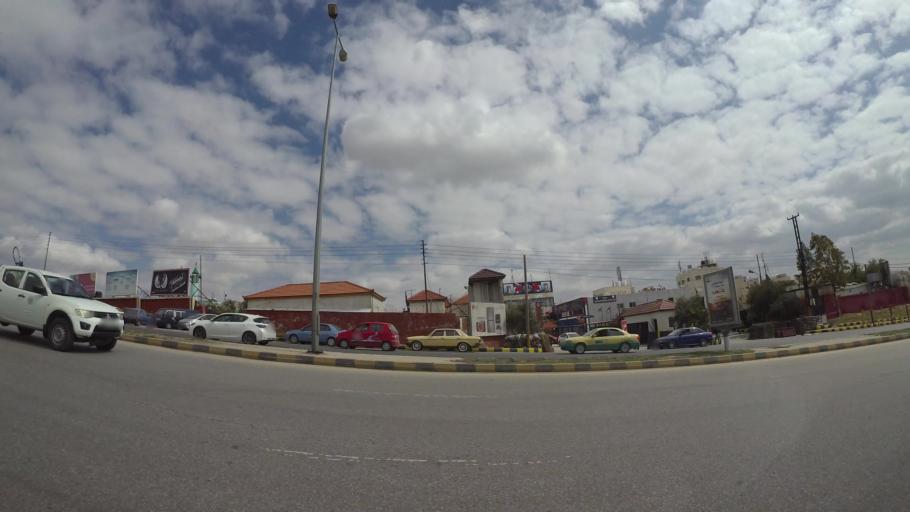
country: JO
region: Amman
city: Amman
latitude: 31.9973
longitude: 35.9185
